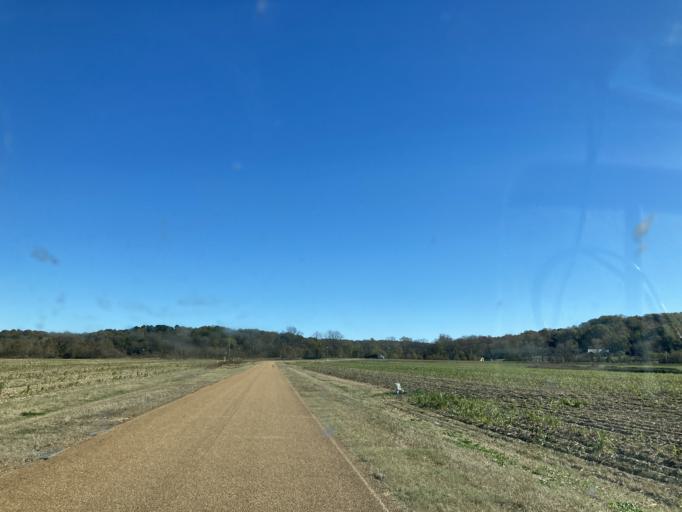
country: US
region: Mississippi
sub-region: Hinds County
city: Lynchburg
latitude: 32.6257
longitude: -90.5774
